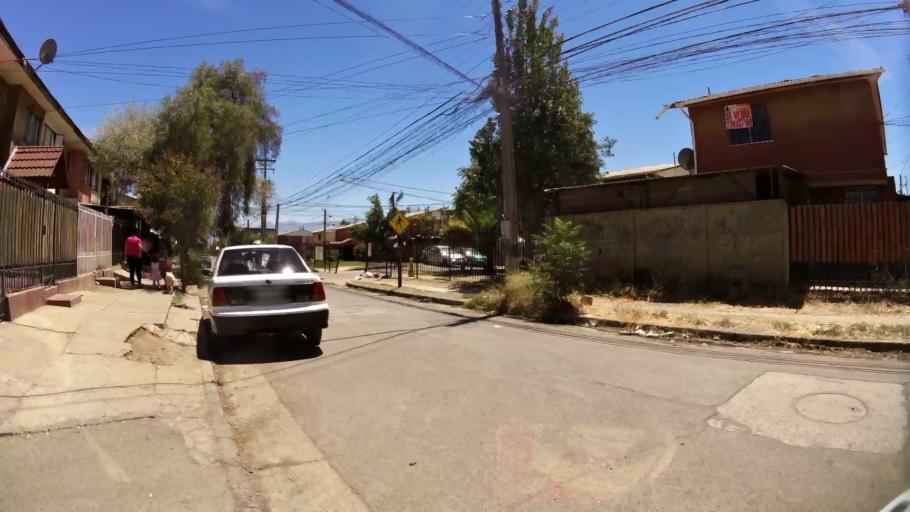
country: CL
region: O'Higgins
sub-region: Provincia de Cachapoal
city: Rancagua
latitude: -34.1620
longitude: -70.7017
